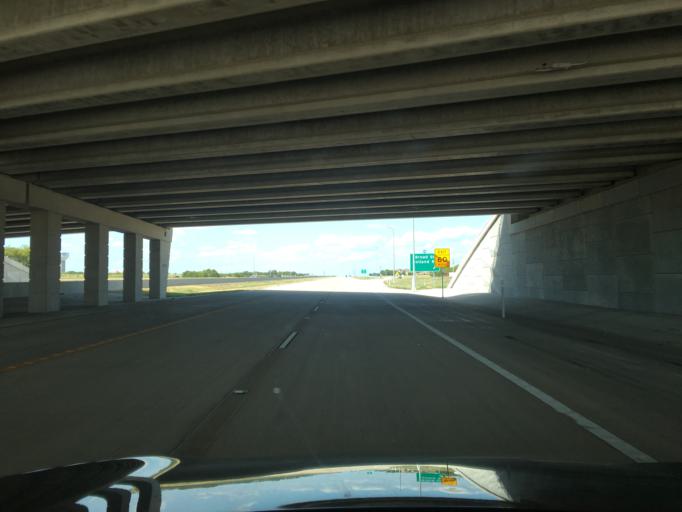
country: US
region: Texas
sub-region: Tarrant County
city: Mansfield
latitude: 32.5604
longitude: -97.0852
